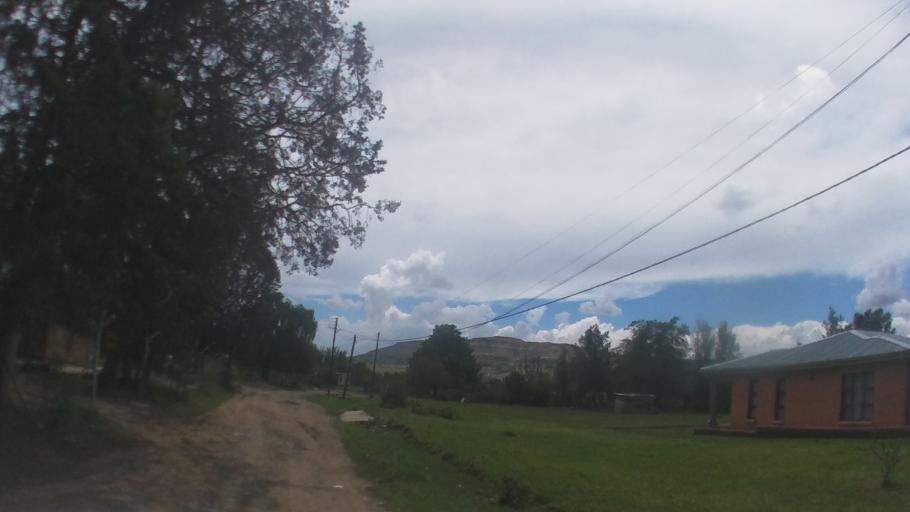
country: LS
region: Maseru
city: Nako
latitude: -29.6224
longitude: 27.5072
